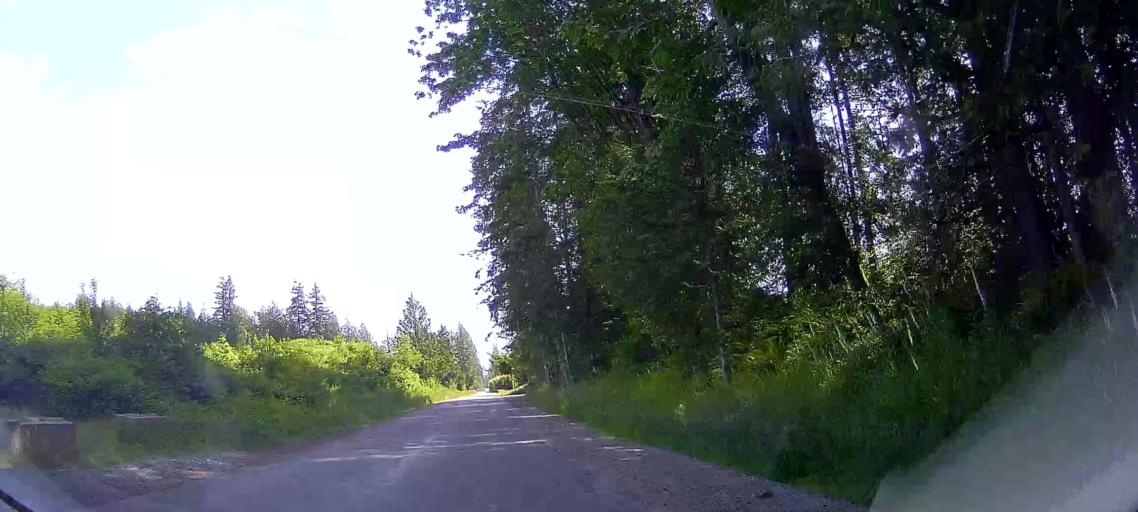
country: US
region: Washington
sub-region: Skagit County
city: Burlington
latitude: 48.5579
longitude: -122.3618
